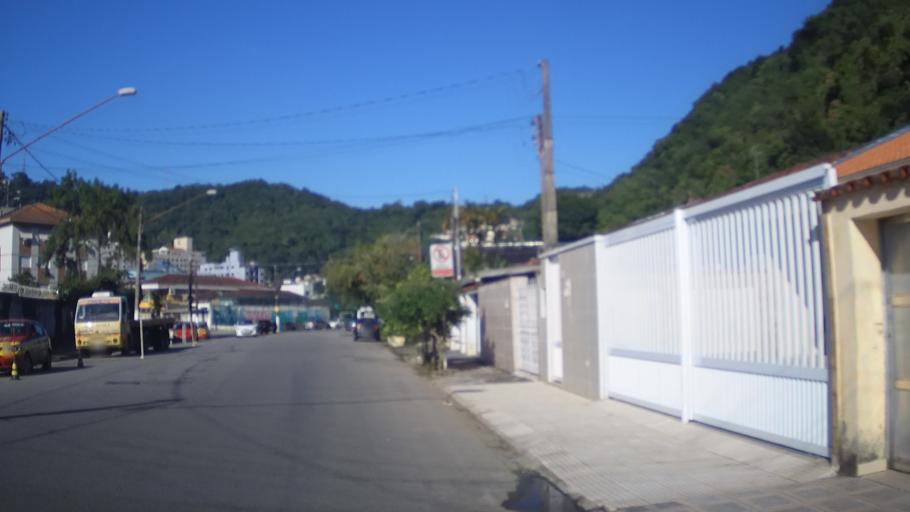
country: BR
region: Sao Paulo
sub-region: Santos
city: Santos
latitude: -23.9505
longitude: -46.3468
